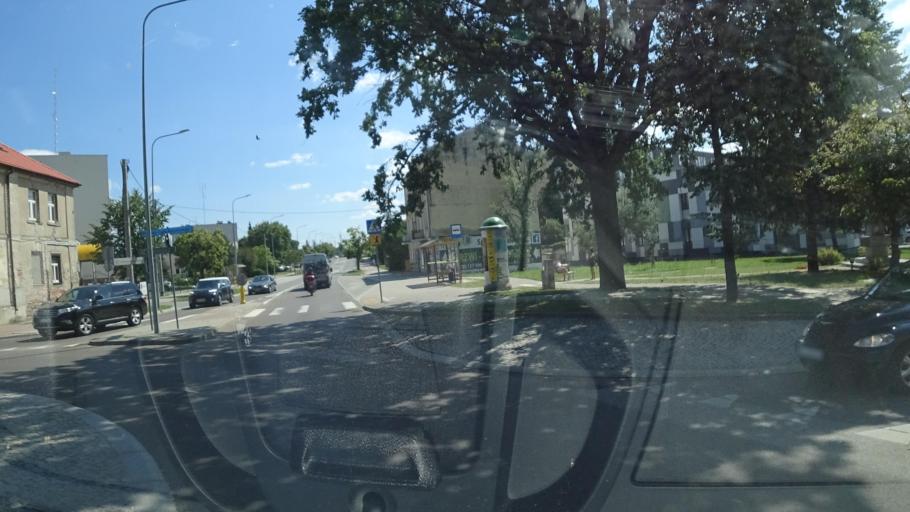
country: PL
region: Podlasie
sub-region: Lomza
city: Lomza
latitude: 53.1744
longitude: 22.0790
